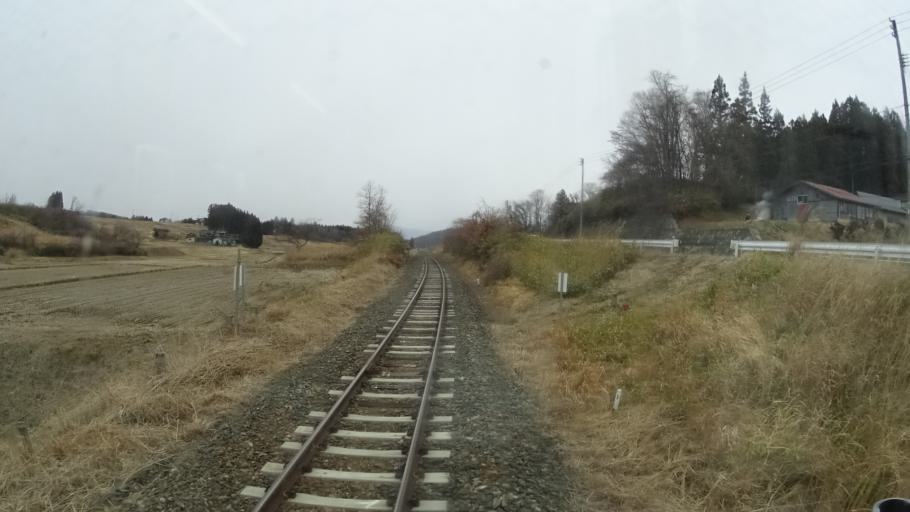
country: JP
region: Iwate
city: Hanamaki
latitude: 39.3983
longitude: 141.2098
